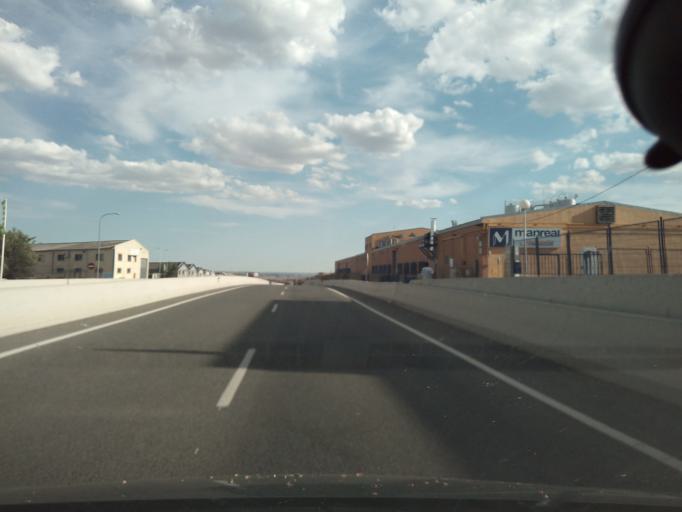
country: ES
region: Madrid
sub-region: Provincia de Madrid
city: Ajalvir
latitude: 40.5125
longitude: -3.4806
